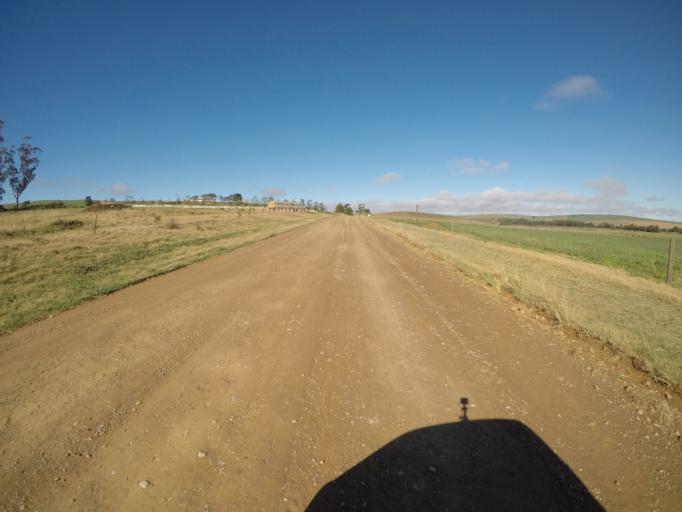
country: ZA
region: Western Cape
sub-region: Overberg District Municipality
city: Caledon
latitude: -34.1072
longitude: 19.7064
